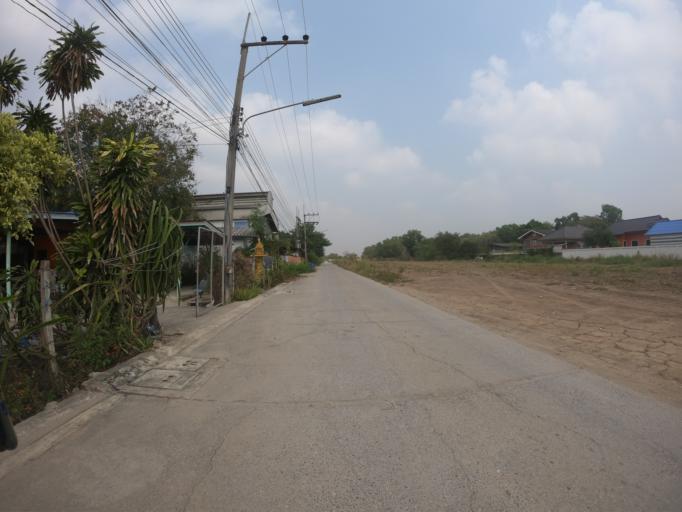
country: TH
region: Pathum Thani
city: Nong Suea
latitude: 14.0635
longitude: 100.8512
